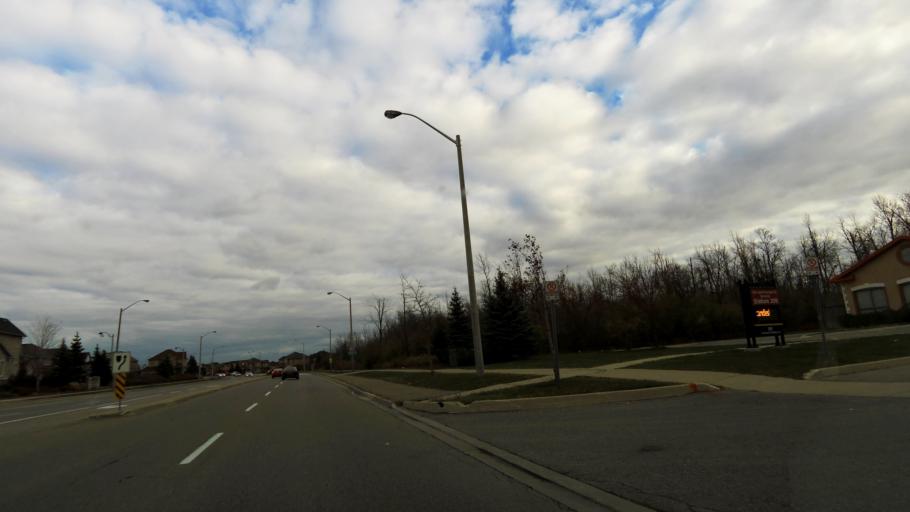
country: CA
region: Ontario
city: Brampton
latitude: 43.7664
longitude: -79.7409
